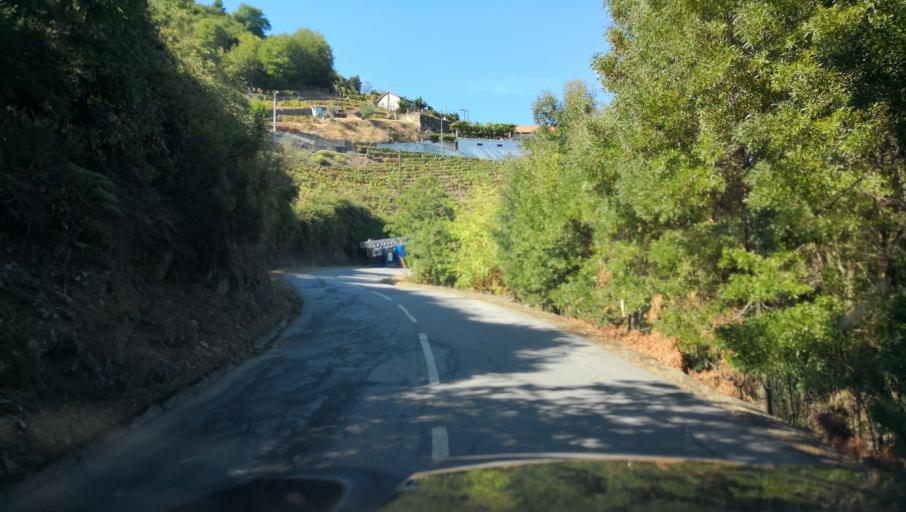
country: PT
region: Vila Real
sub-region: Santa Marta de Penaguiao
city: Santa Marta de Penaguiao
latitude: 41.2250
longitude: -7.7855
